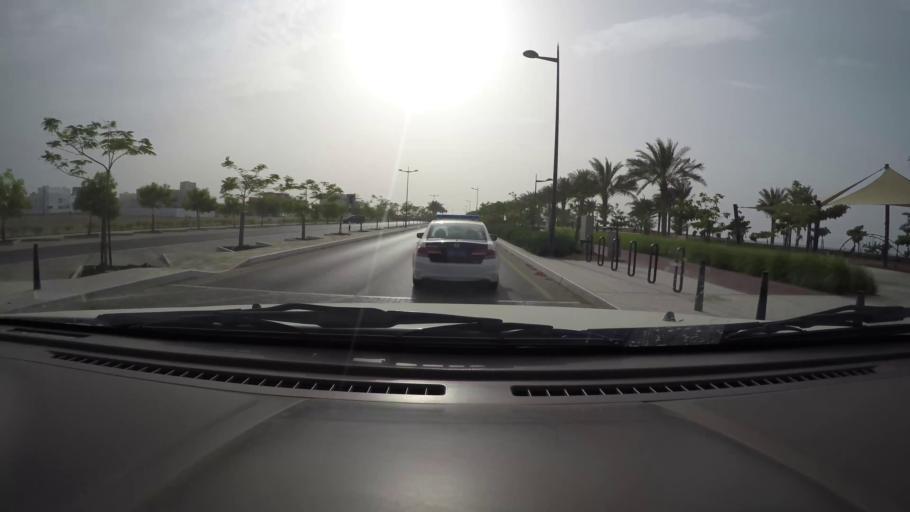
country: OM
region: Muhafazat Masqat
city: As Sib al Jadidah
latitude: 23.6954
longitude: 58.1550
